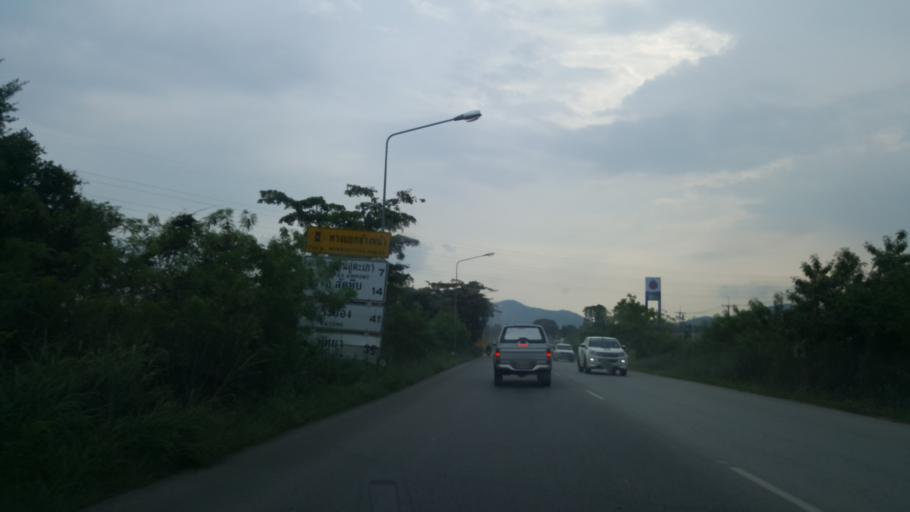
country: TH
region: Rayong
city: Ban Chang
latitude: 12.7312
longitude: 100.9855
